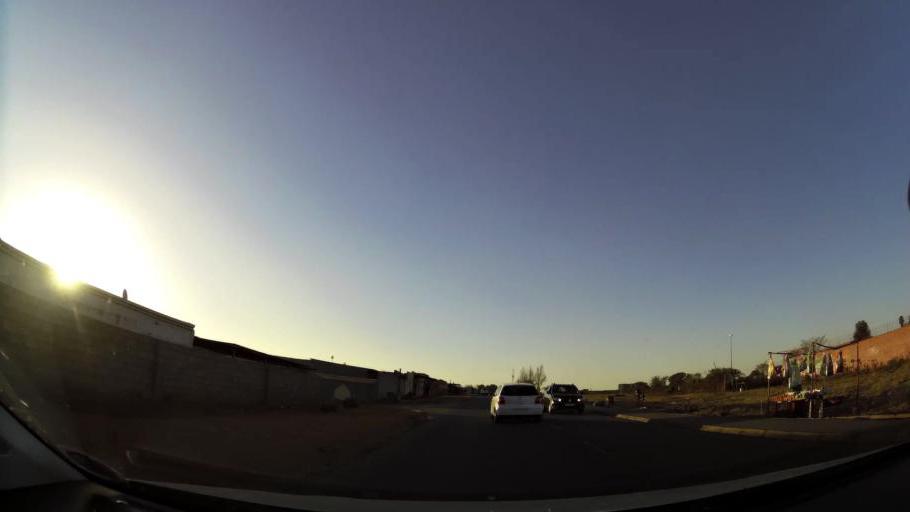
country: ZA
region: Gauteng
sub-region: Ekurhuleni Metropolitan Municipality
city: Tembisa
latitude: -26.0099
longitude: 28.2140
